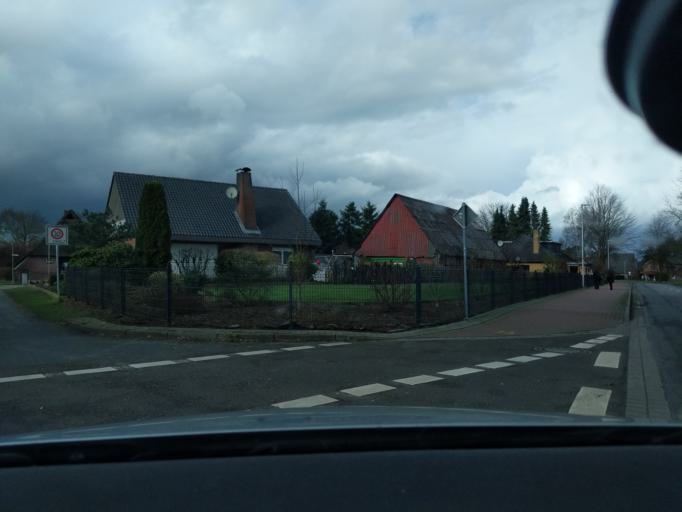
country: DE
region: Lower Saxony
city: Heinbockel
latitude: 53.5748
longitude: 9.3283
